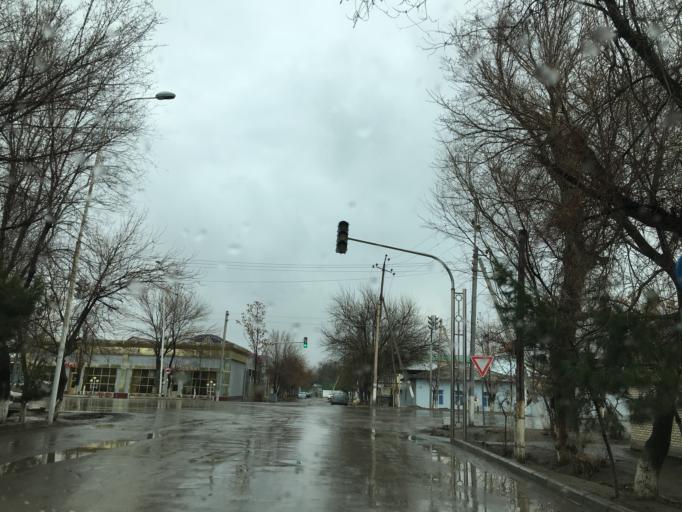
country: TM
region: Mary
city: Yoloeten
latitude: 37.2940
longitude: 62.3621
